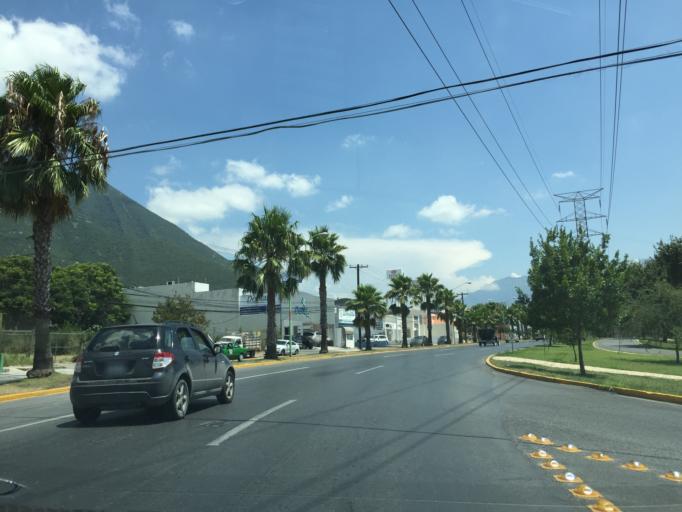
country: MX
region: Nuevo Leon
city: Guadalupe
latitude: 25.6463
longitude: -100.2681
